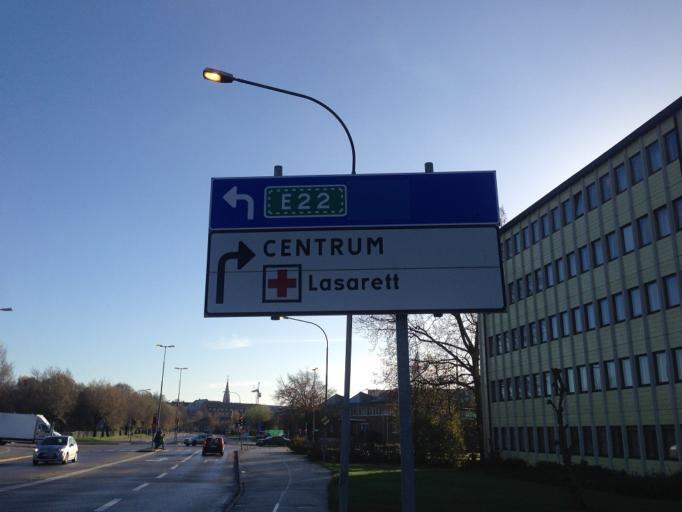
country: SE
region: Skane
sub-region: Lunds Kommun
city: Lund
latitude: 55.7127
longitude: 13.1791
